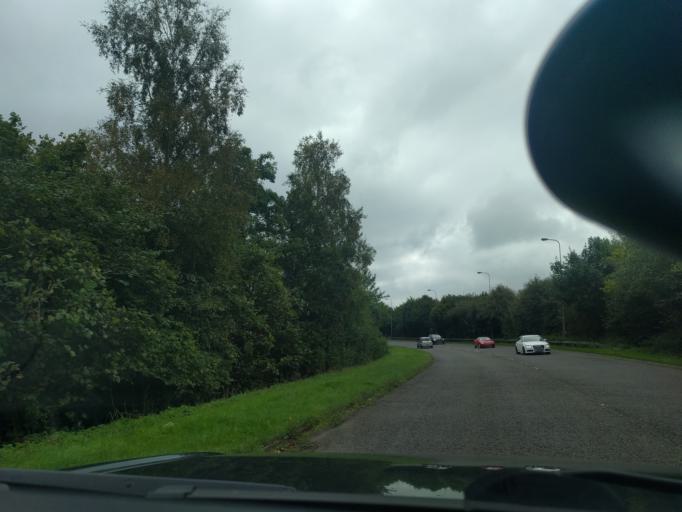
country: GB
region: England
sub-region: Wiltshire
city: Chippenham
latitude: 51.4548
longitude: -2.1185
